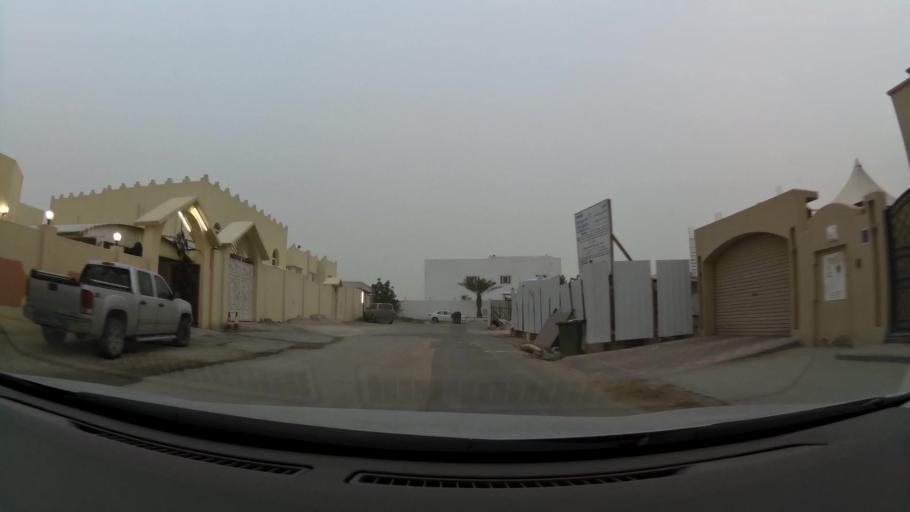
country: QA
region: Baladiyat ad Dawhah
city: Doha
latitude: 25.2284
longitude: 51.4979
